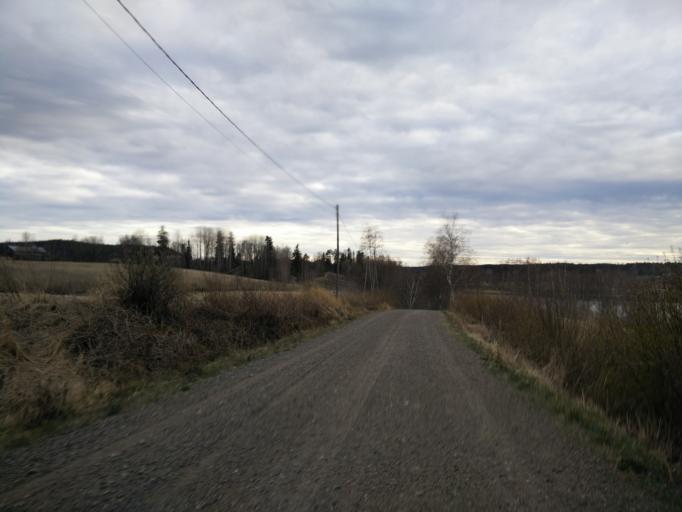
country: FI
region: Pirkanmaa
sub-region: Tampere
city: Orivesi
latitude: 61.7071
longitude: 24.3175
